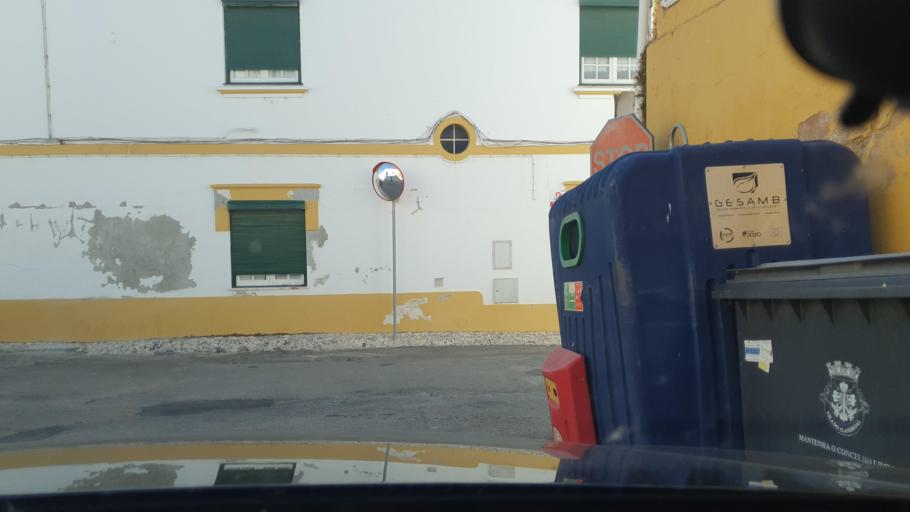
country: PT
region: Evora
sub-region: Alandroal
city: Alandroal
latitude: 38.7018
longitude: -7.4025
